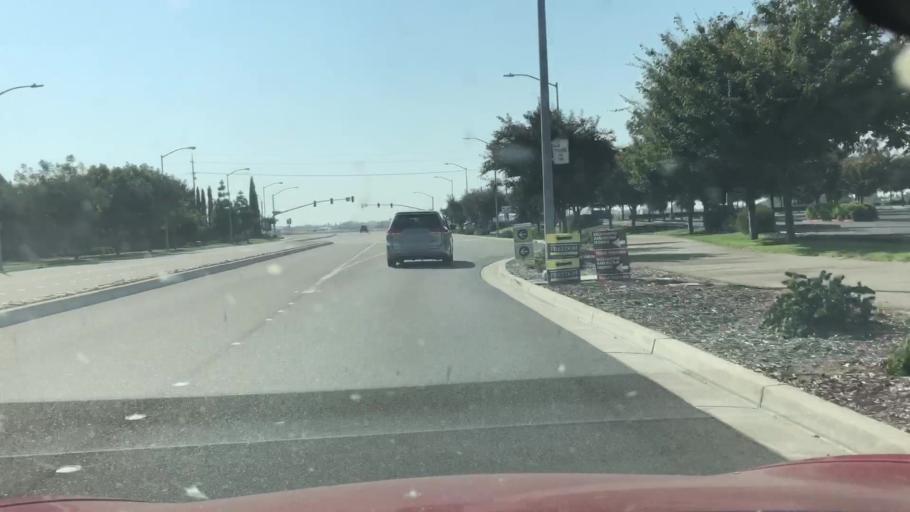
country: US
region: California
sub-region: San Joaquin County
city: Manteca
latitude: 37.7793
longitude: -121.2316
